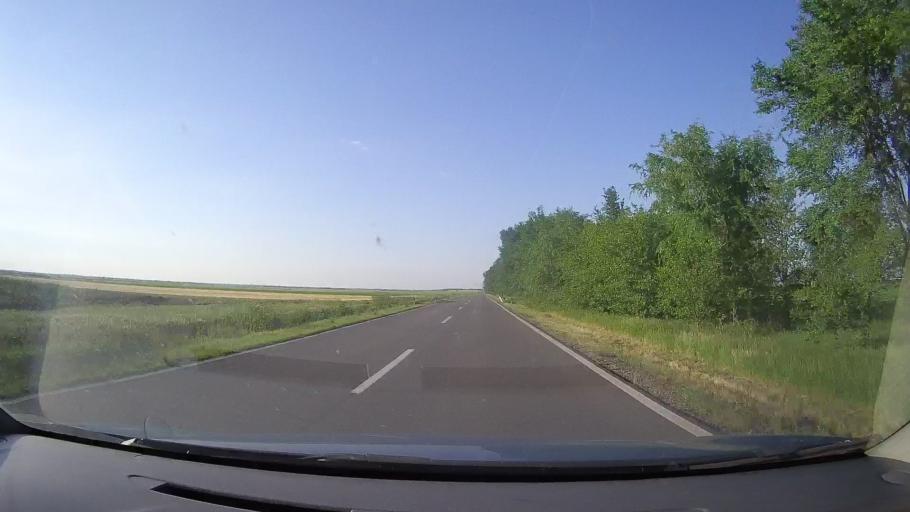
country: RS
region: Autonomna Pokrajina Vojvodina
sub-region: Juznobanatski Okrug
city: Vrsac
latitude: 45.1782
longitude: 21.2952
